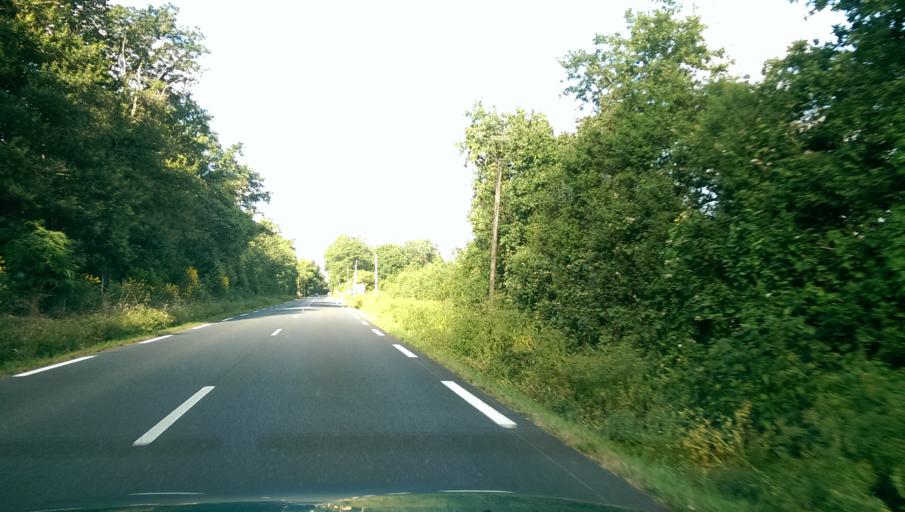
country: FR
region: Pays de la Loire
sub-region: Departement de la Vendee
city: Rocheserviere
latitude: 46.9286
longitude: -1.5233
